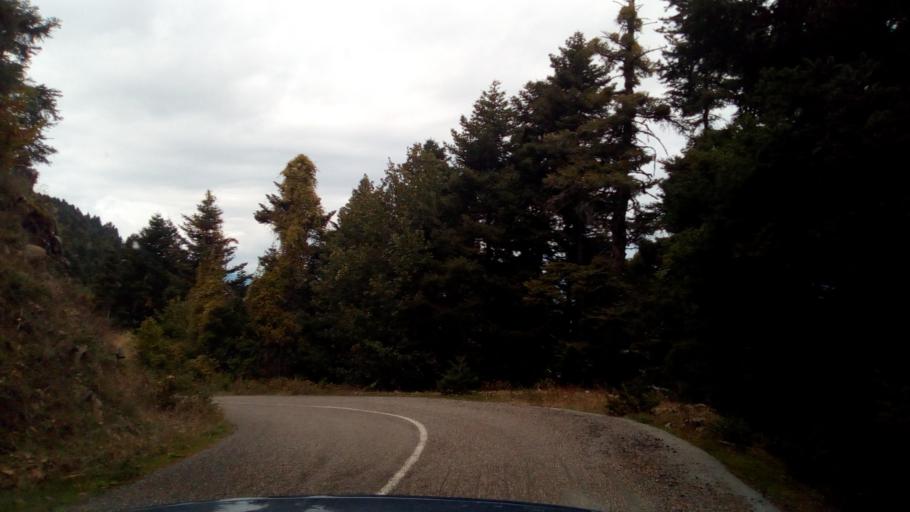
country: GR
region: Central Greece
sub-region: Nomos Fokidos
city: Lidoriki
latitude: 38.4778
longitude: 22.0665
